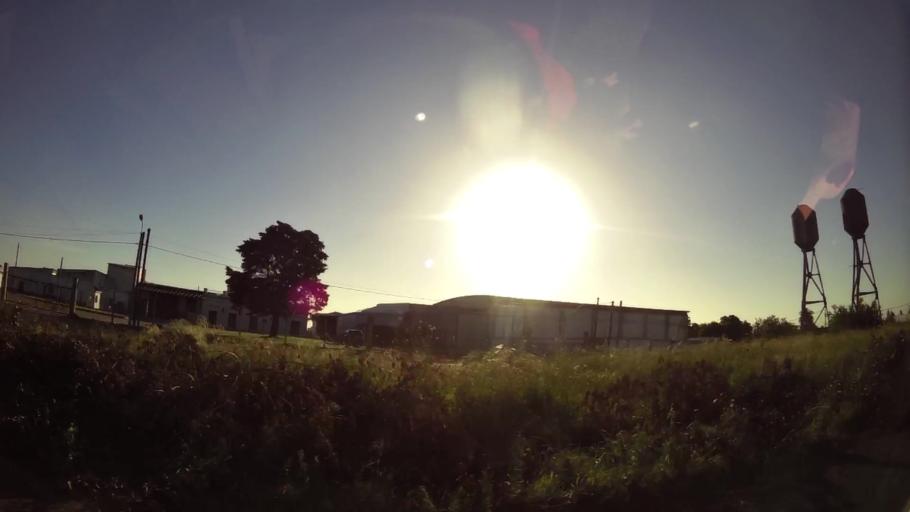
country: UY
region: Canelones
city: La Paz
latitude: -34.8294
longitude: -56.2449
